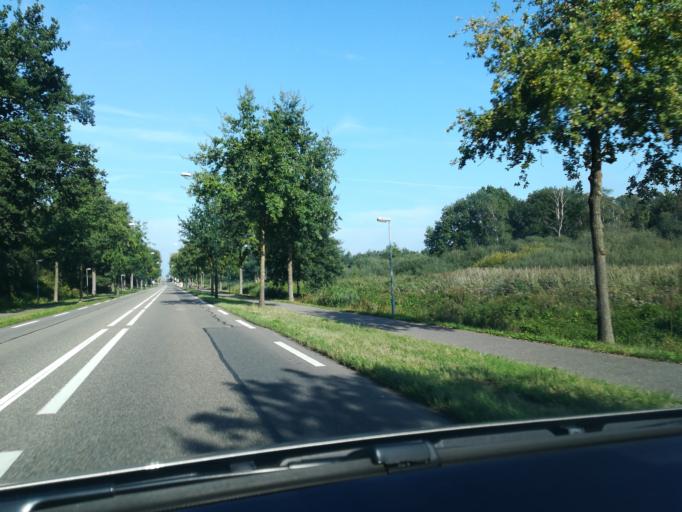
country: NL
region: North Brabant
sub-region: Gemeente Waalre
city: Waalre
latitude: 51.4006
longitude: 5.4294
